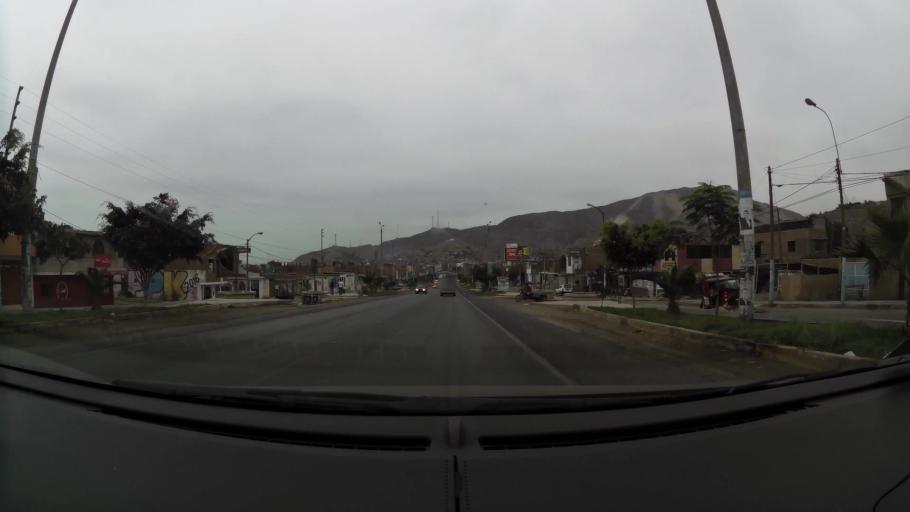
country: PE
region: Ancash
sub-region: Provincia de Santa
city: Coishco
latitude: -9.0255
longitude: -78.6160
